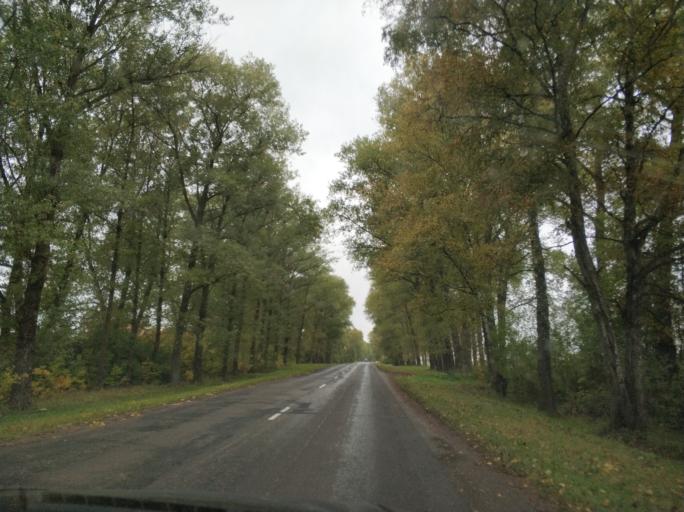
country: BY
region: Vitebsk
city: Polatsk
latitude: 55.4320
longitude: 28.9904
